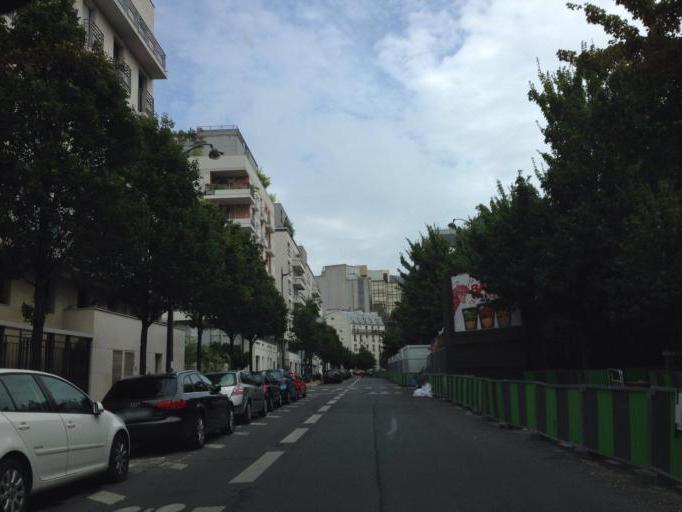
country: FR
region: Ile-de-France
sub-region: Departement des Hauts-de-Seine
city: Montrouge
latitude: 48.8373
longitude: 2.3132
